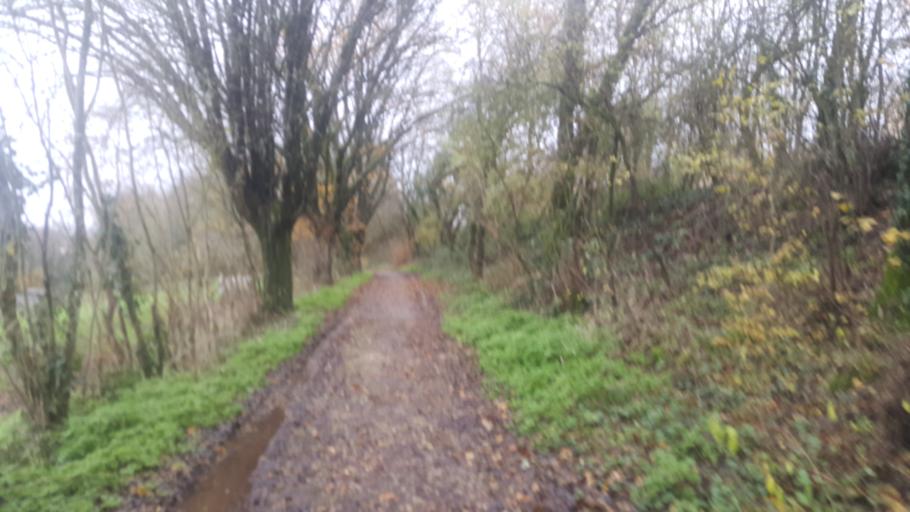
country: FR
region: Poitou-Charentes
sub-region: Departement des Deux-Sevres
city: Melle
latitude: 46.2296
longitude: -0.1483
